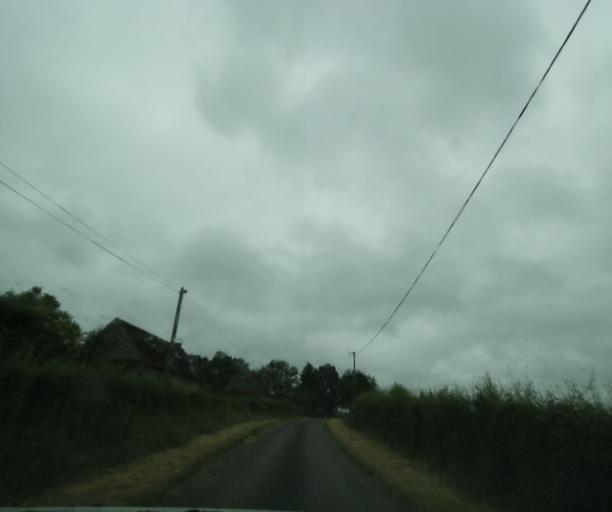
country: FR
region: Bourgogne
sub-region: Departement de Saone-et-Loire
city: Palinges
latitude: 46.5208
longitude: 4.2125
